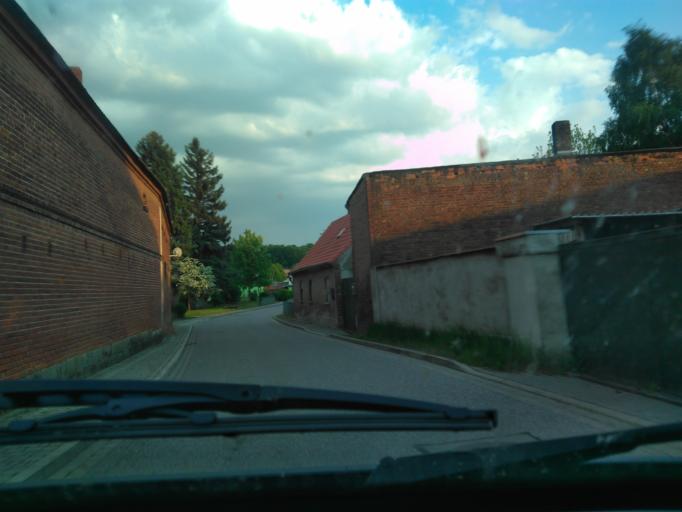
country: DE
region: Saxony-Anhalt
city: Wethau
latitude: 51.1206
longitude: 11.8740
